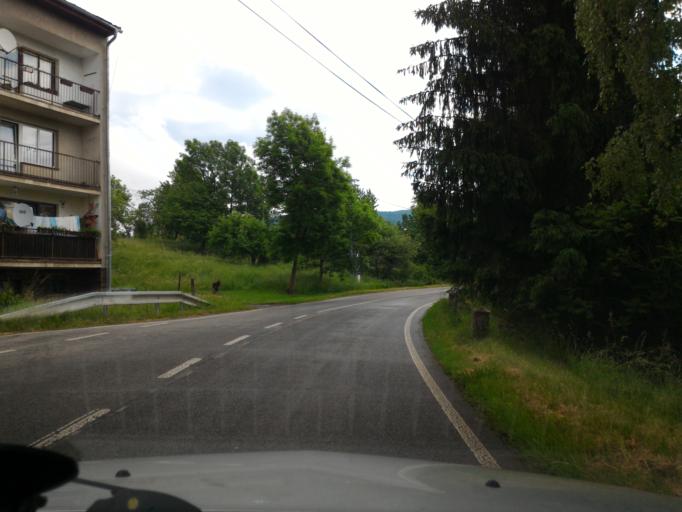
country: CZ
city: Osecna
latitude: 50.7393
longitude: 14.9092
